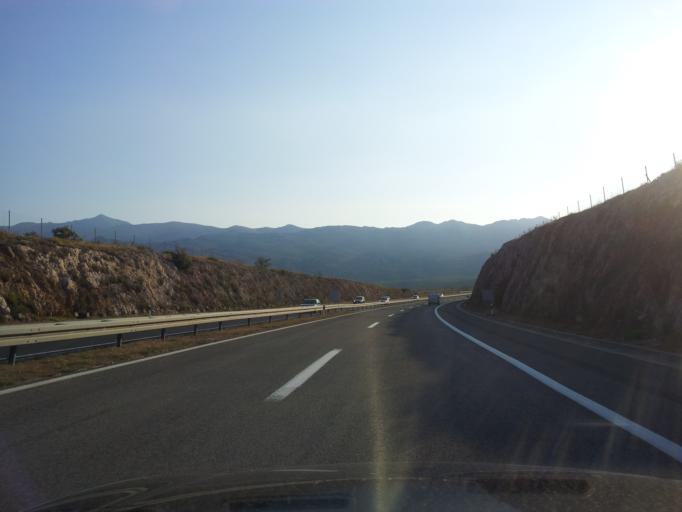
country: HR
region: Zadarska
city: Posedarje
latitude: 44.2341
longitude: 15.5143
